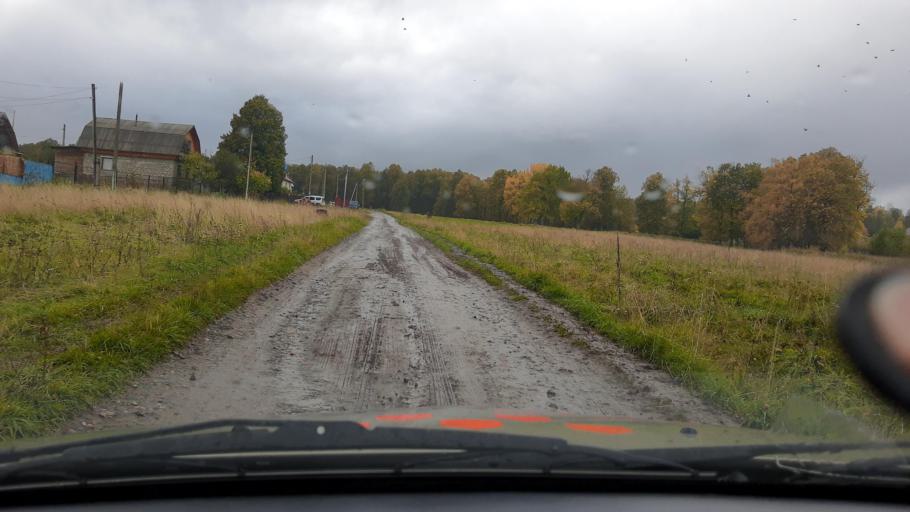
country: RU
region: Bashkortostan
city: Kudeyevskiy
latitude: 54.8759
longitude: 56.6283
